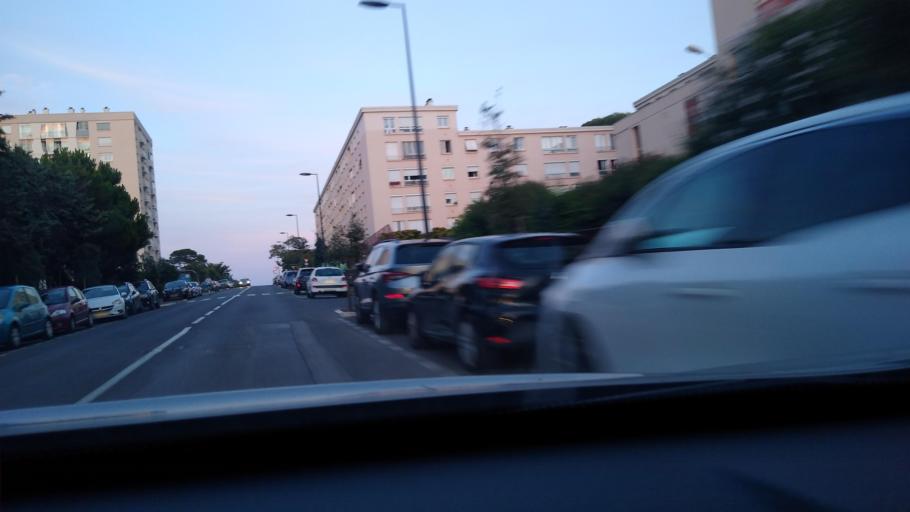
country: FR
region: Languedoc-Roussillon
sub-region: Departement de l'Herault
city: Sete
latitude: 43.4069
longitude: 3.6835
